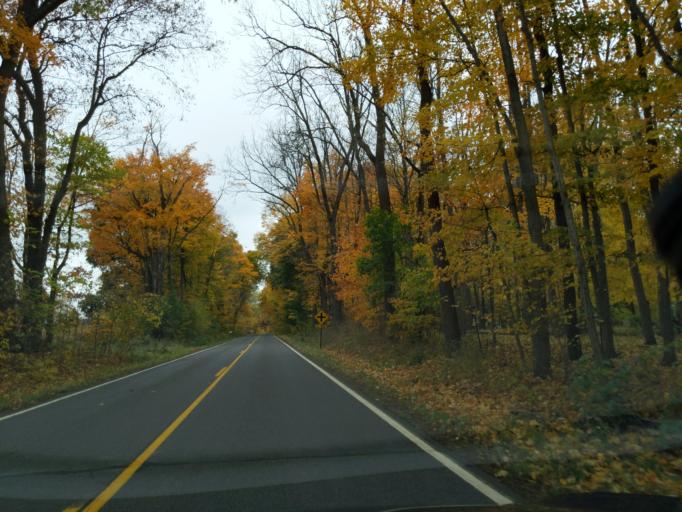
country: US
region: Michigan
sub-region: Eaton County
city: Eaton Rapids
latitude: 42.3812
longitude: -84.6005
